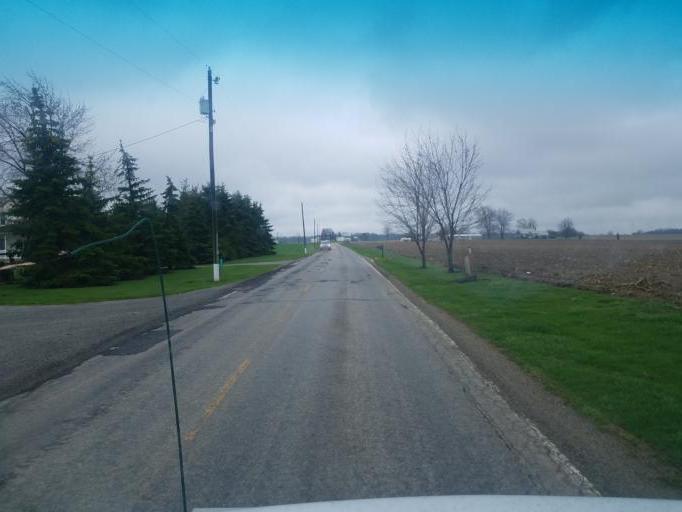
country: US
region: Ohio
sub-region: Richland County
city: Shelby
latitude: 40.9328
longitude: -82.6441
